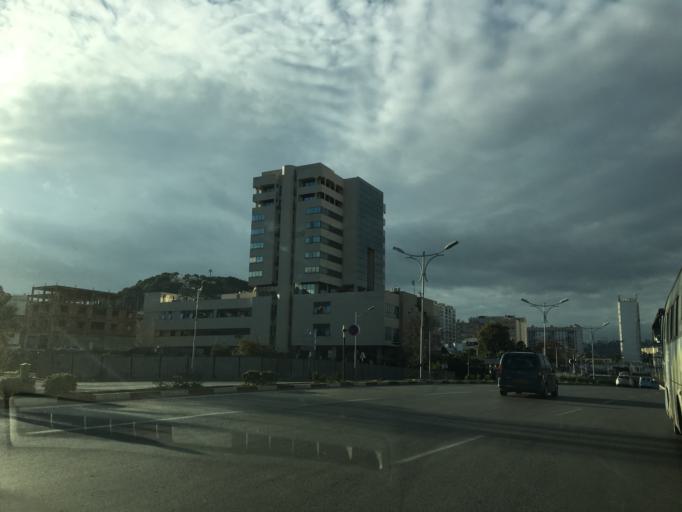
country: DZ
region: Alger
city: Algiers
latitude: 36.7426
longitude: 3.0864
